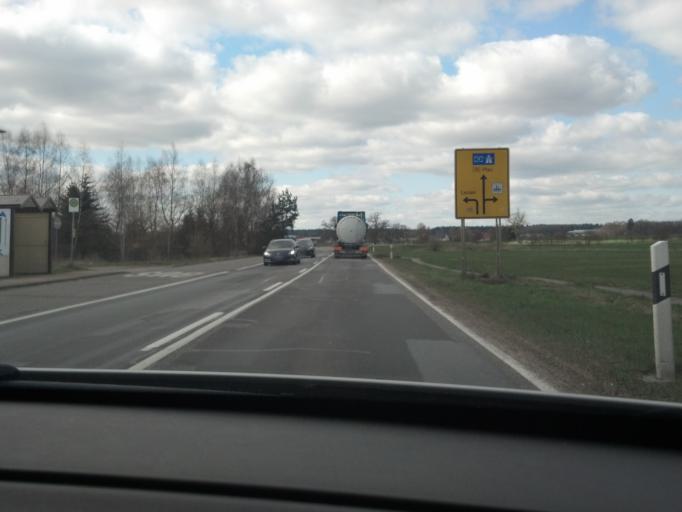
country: DE
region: Mecklenburg-Vorpommern
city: Malchow
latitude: 53.3662
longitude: 12.4788
